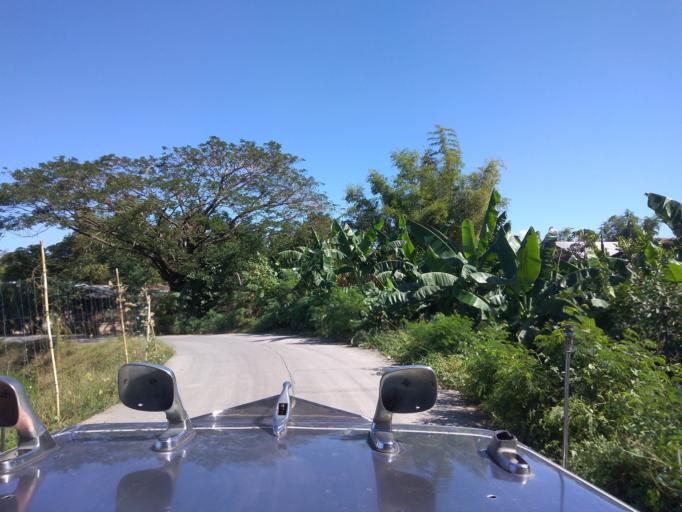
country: PH
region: Central Luzon
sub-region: Province of Pampanga
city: Batasan Bata
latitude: 15.1637
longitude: 120.9198
